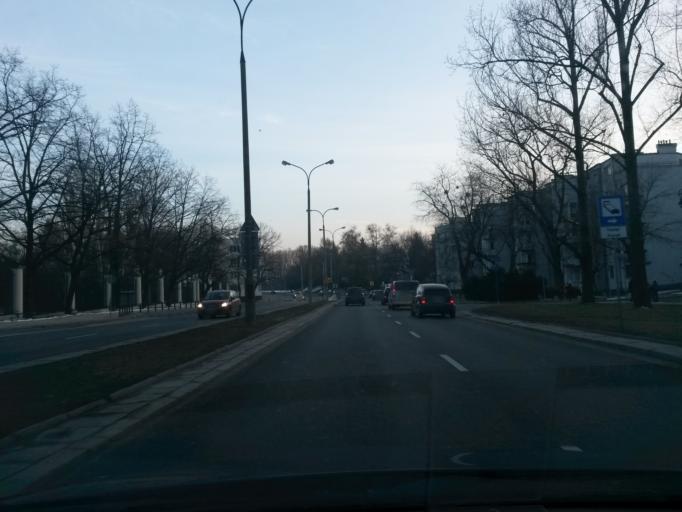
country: PL
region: Masovian Voivodeship
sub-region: Warszawa
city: Mokotow
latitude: 52.2106
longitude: 21.0250
